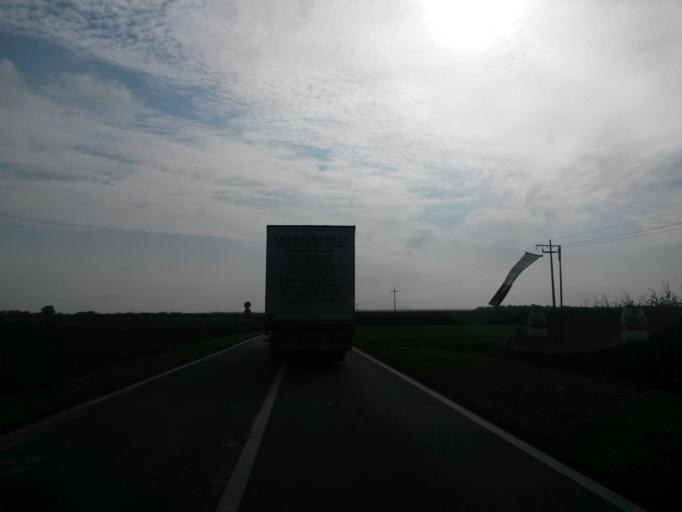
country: HR
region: Vukovarsko-Srijemska
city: Lovas
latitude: 45.2459
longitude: 19.2264
